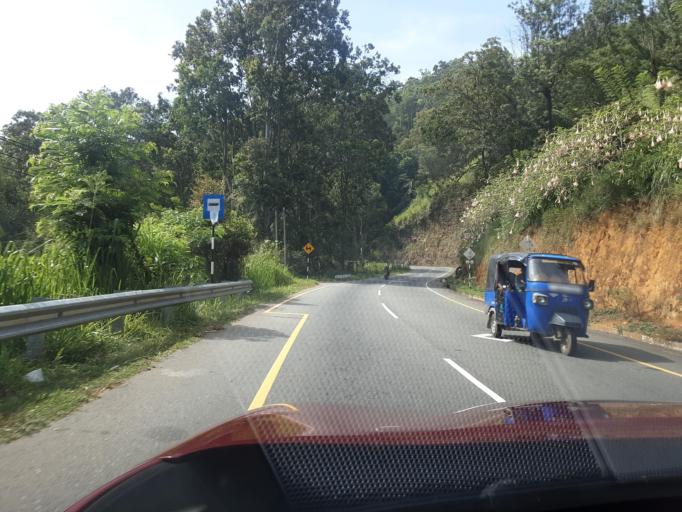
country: LK
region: Uva
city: Badulla
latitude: 6.9654
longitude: 81.0917
